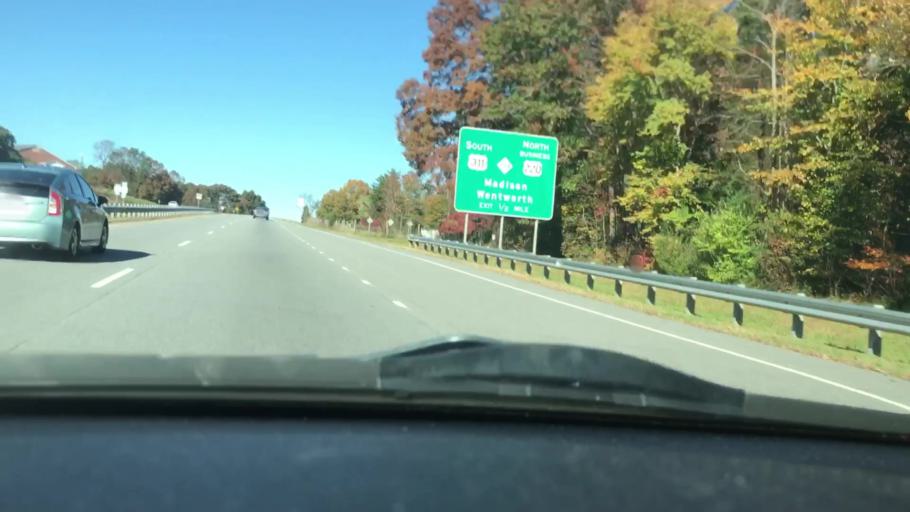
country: US
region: North Carolina
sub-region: Rockingham County
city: Madison
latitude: 36.3662
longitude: -79.9443
